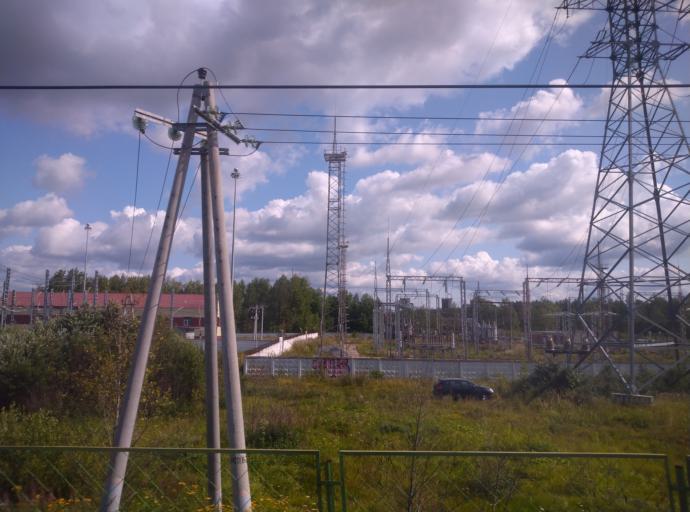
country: RU
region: Leningrad
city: Krasnyy Bor
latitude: 59.6763
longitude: 30.7070
